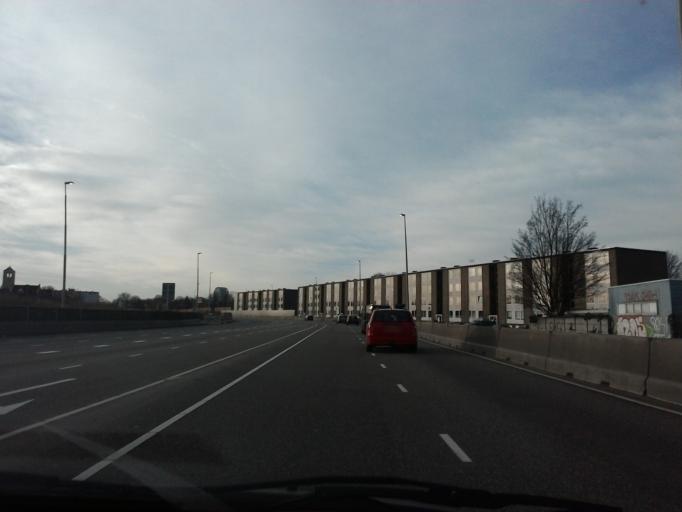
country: NL
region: Limburg
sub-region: Gemeente Maastricht
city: Maastricht
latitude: 50.8581
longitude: 5.7119
